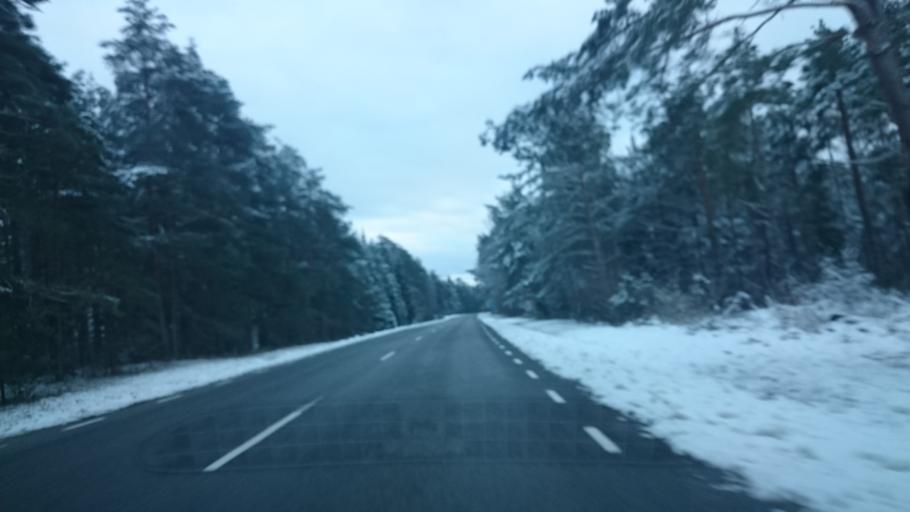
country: EE
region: Saare
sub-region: Kuressaare linn
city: Kuressaare
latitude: 58.3932
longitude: 22.6476
